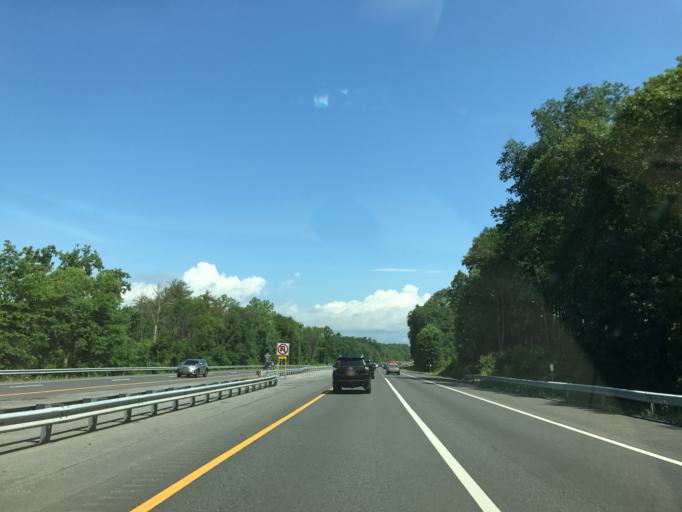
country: US
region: New York
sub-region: Ulster County
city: Tillson
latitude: 41.8180
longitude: -74.0563
